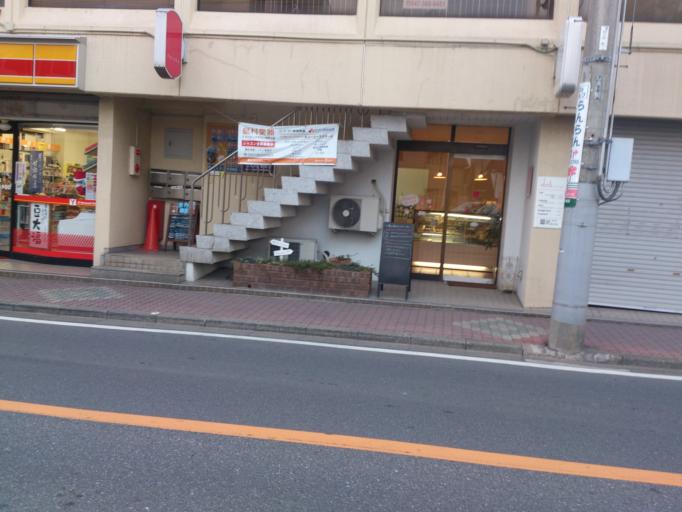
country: JP
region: Chiba
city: Matsudo
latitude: 35.7898
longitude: 139.9297
